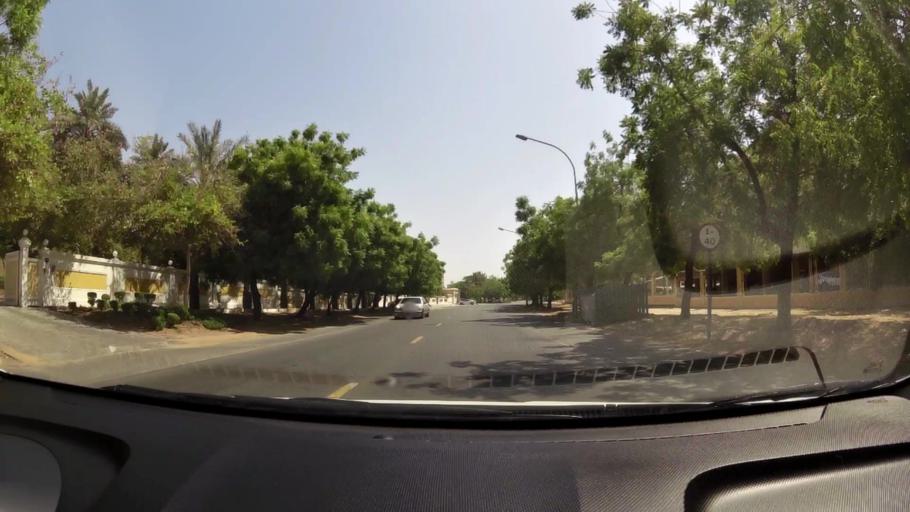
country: AE
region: Ash Shariqah
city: Sharjah
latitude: 25.2758
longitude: 55.3633
